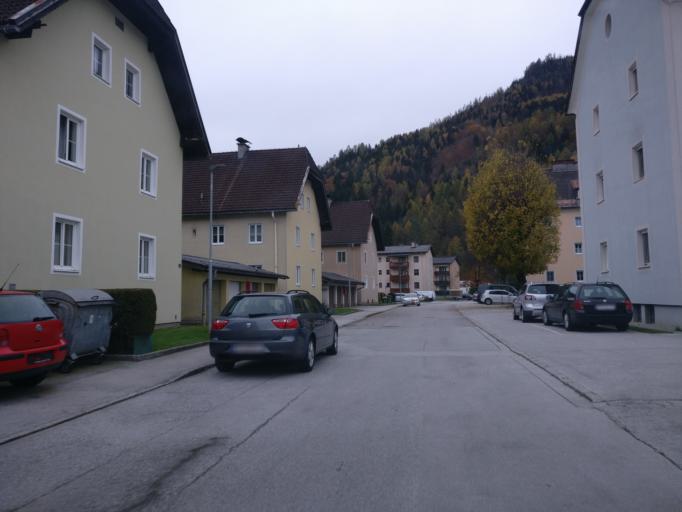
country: AT
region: Salzburg
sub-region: Politischer Bezirk Sankt Johann im Pongau
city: Bischofshofen
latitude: 47.4252
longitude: 13.2171
